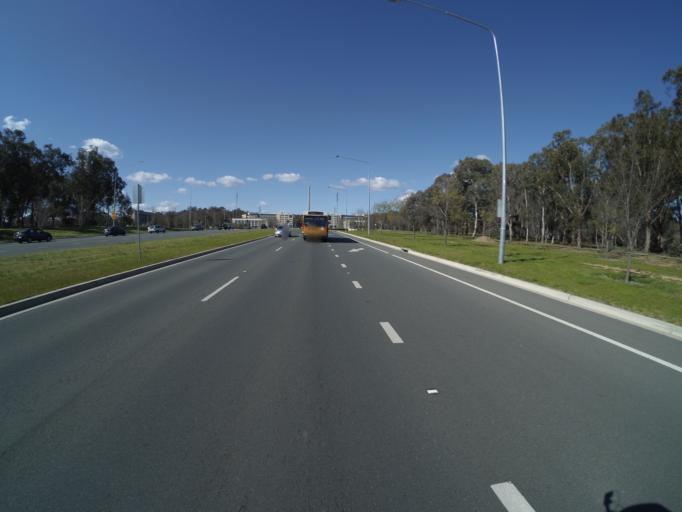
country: AU
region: Australian Capital Territory
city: Forrest
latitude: -35.2999
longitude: 149.1462
